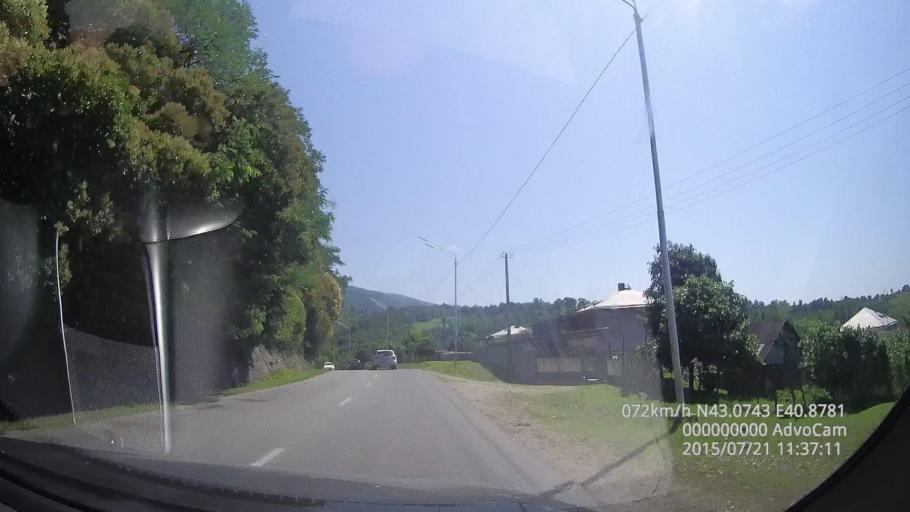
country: GE
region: Abkhazia
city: Stantsiya Novyy Afon
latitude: 43.0743
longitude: 40.8789
